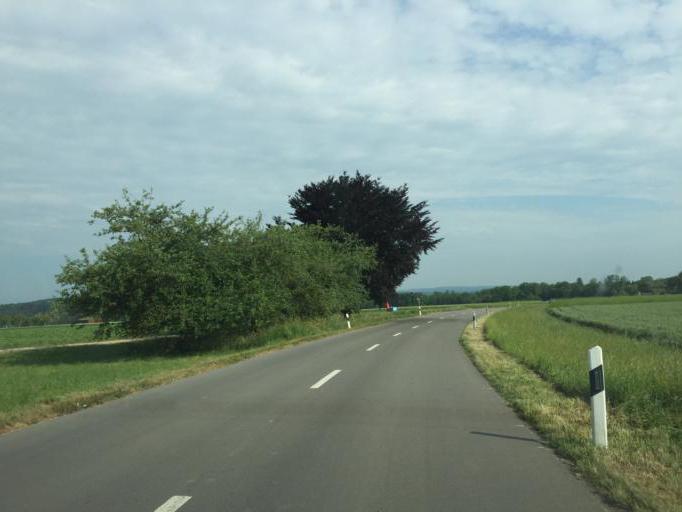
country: CH
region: Zurich
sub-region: Bezirk Buelach
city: Freienstein
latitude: 47.5835
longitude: 8.6062
